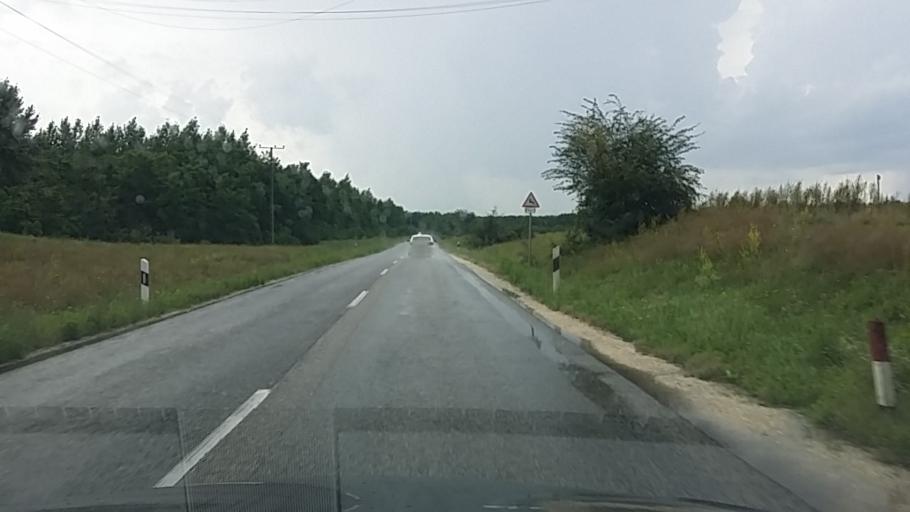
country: HU
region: Pest
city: Inarcs
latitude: 47.3282
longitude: 19.3053
